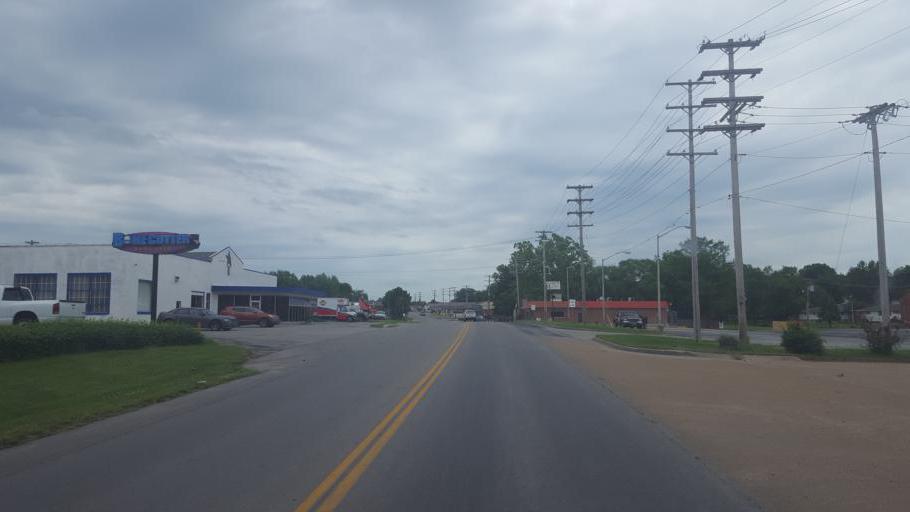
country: US
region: Missouri
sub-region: Moniteau County
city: California
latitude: 38.6279
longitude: -92.5738
